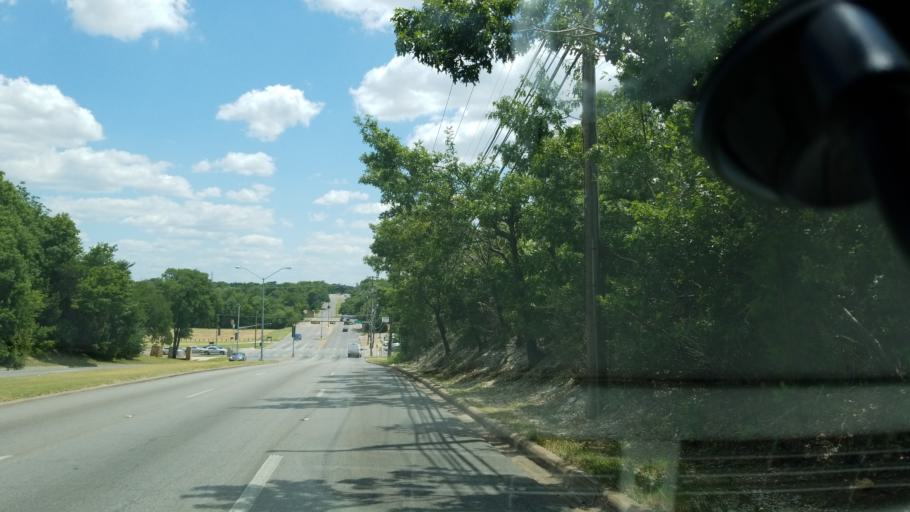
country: US
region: Texas
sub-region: Dallas County
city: Cockrell Hill
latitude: 32.7072
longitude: -96.8572
